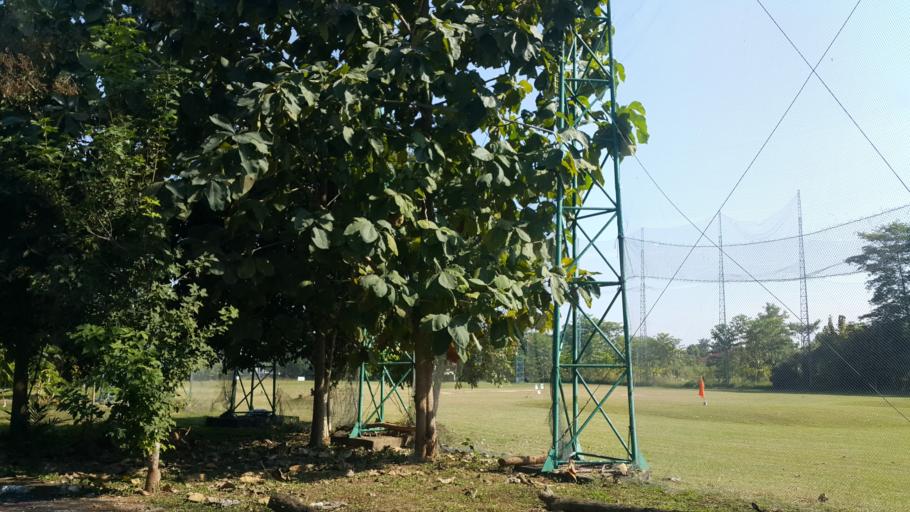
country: TH
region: Chiang Mai
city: Hang Dong
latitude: 18.7410
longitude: 98.9386
